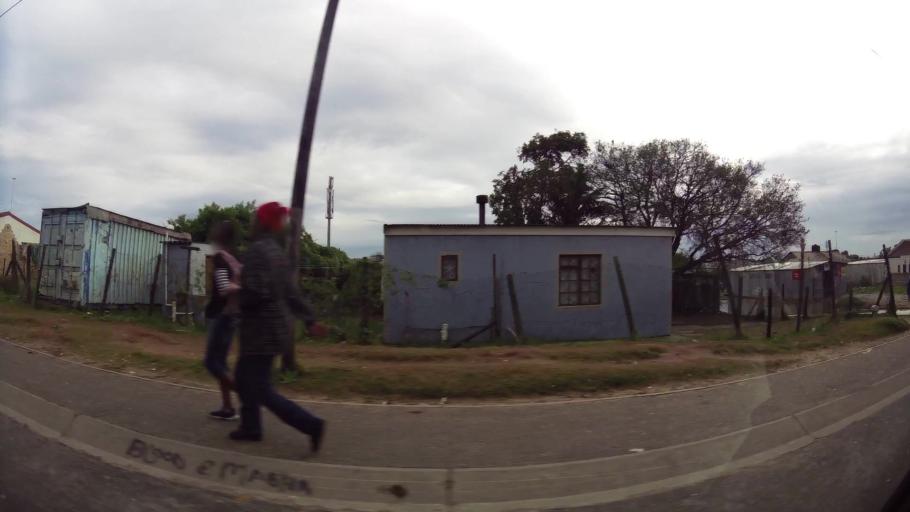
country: ZA
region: Eastern Cape
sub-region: Nelson Mandela Bay Metropolitan Municipality
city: Port Elizabeth
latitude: -33.9898
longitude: 25.5888
